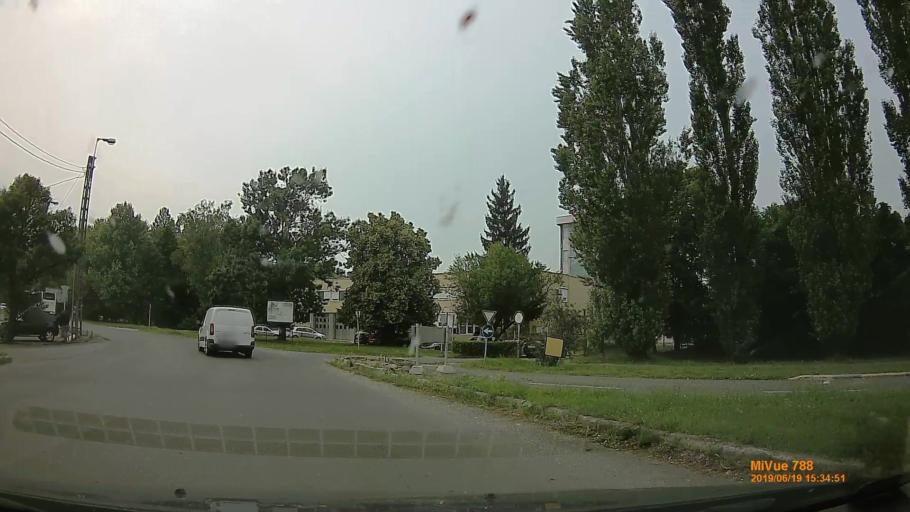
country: HU
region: Baranya
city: Szigetvar
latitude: 46.0485
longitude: 17.8192
